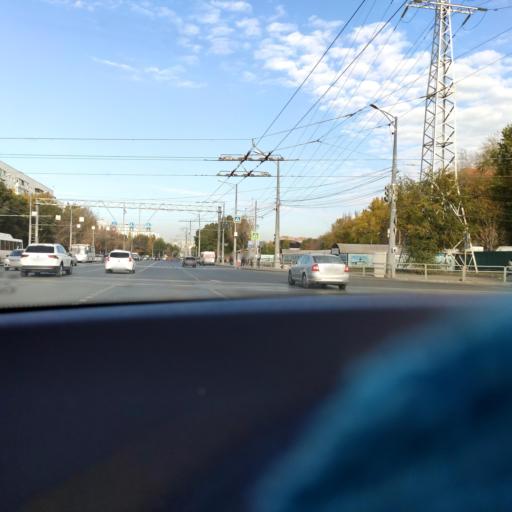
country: RU
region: Samara
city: Samara
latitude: 53.2429
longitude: 50.2099
